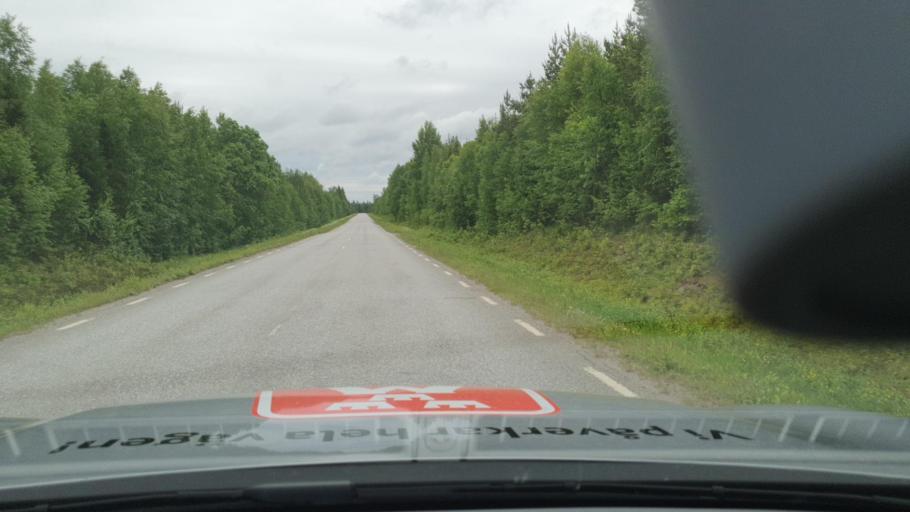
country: SE
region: Norrbotten
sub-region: Lulea Kommun
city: Ranea
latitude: 65.8710
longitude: 22.2246
